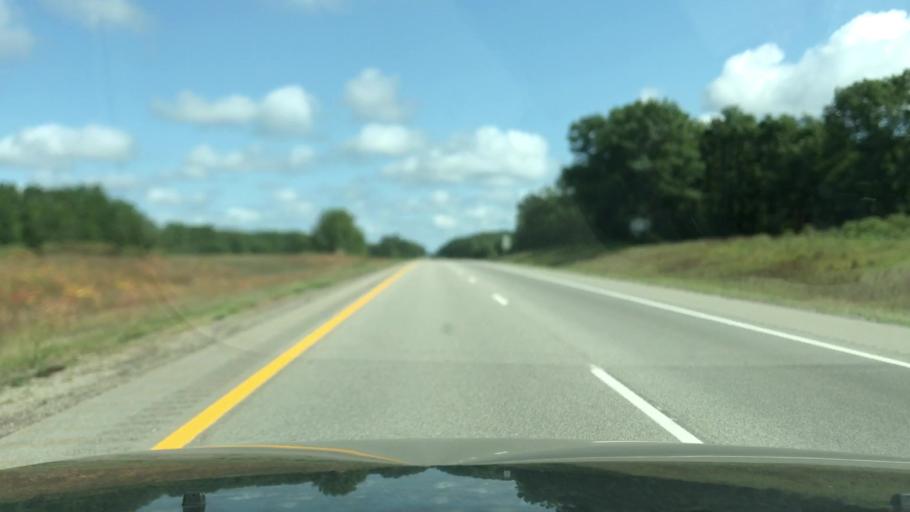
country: US
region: Michigan
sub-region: Montcalm County
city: Howard City
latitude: 43.5011
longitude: -85.4860
